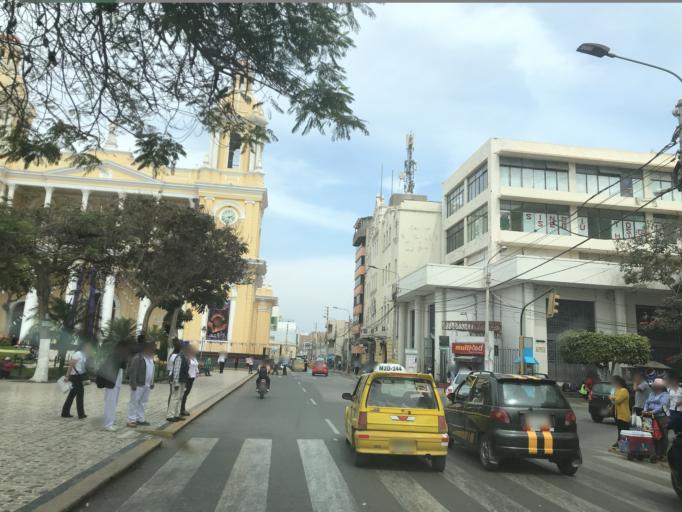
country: PE
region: Lambayeque
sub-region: Provincia de Chiclayo
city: Chiclayo
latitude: -6.7719
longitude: -79.8387
